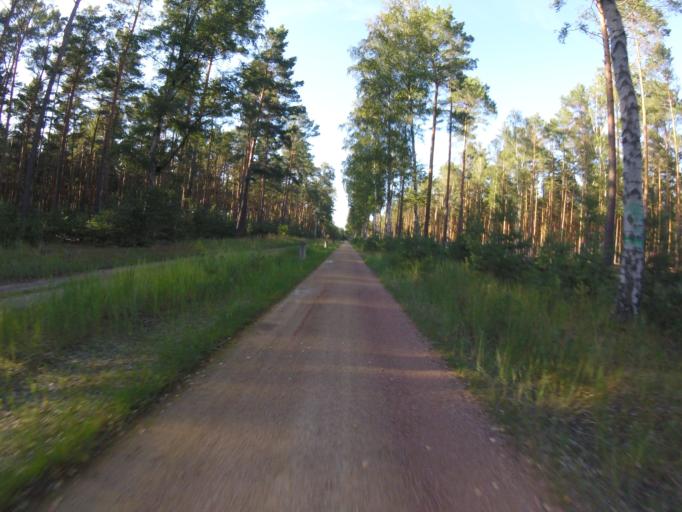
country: DE
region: Brandenburg
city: Munchehofe
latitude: 52.1920
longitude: 13.7620
